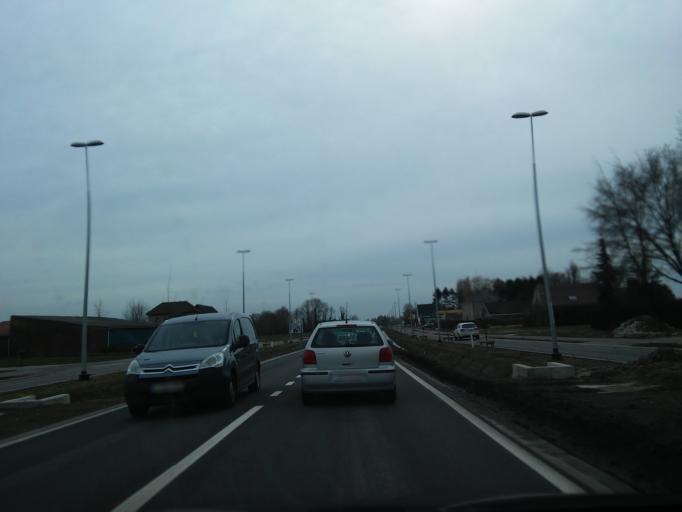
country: BE
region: Flanders
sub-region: Provincie Oost-Vlaanderen
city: Hamme
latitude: 51.1307
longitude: 4.1452
